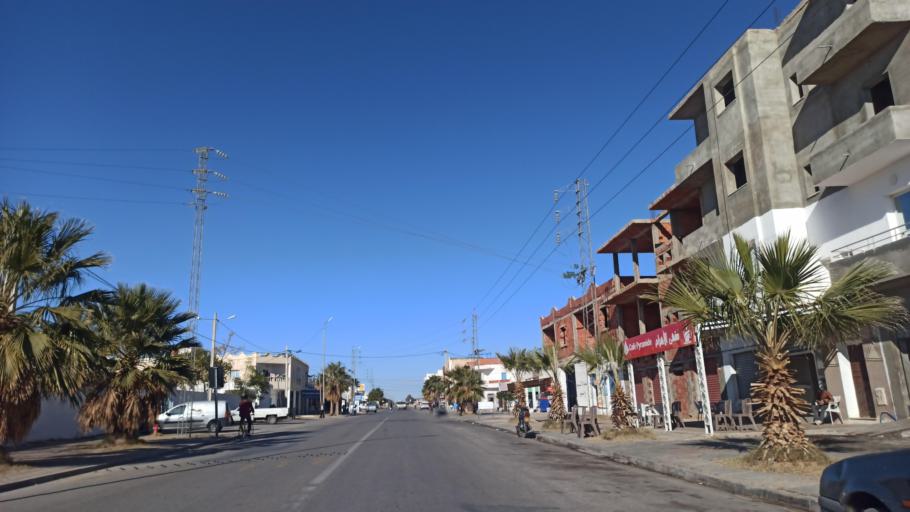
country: TN
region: Sidi Bu Zayd
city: Jilma
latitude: 35.2777
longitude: 9.4189
